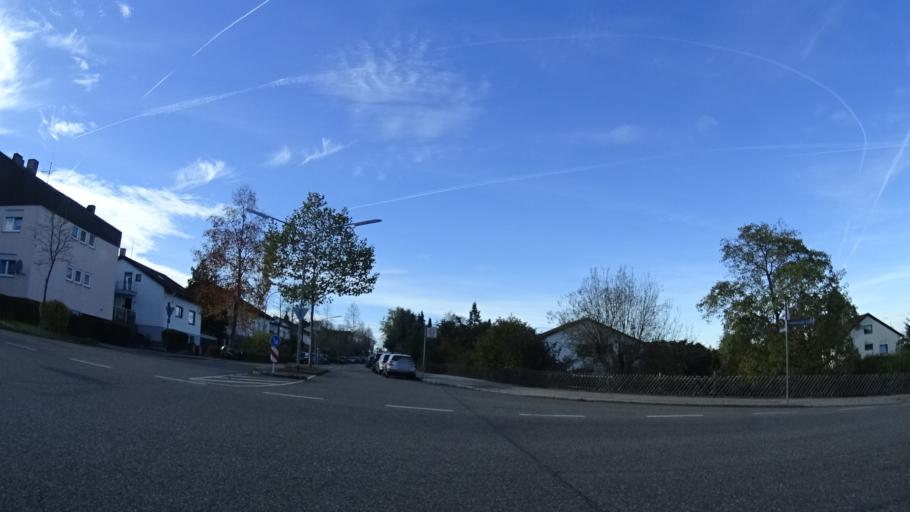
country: DE
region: Baden-Wuerttemberg
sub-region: Karlsruhe Region
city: Pforzheim
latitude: 48.8814
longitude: 8.7139
